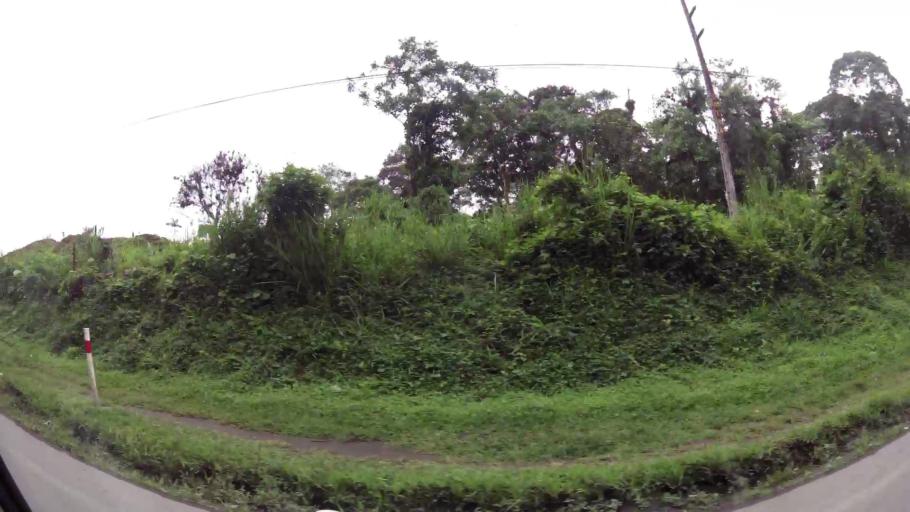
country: EC
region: Santo Domingo de los Tsachilas
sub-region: Canton Santo Domingo de los Colorados
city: Santo Domingo de los Colorados
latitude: -0.2365
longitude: -79.1547
